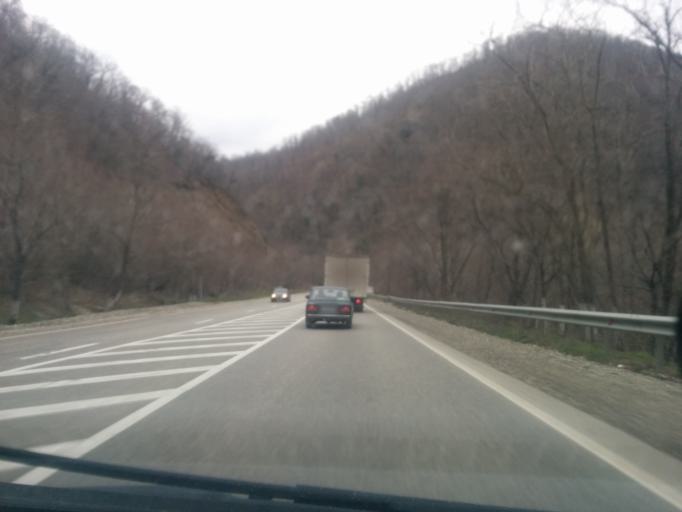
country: RU
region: Krasnodarskiy
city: Nebug
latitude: 44.1763
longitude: 38.9577
